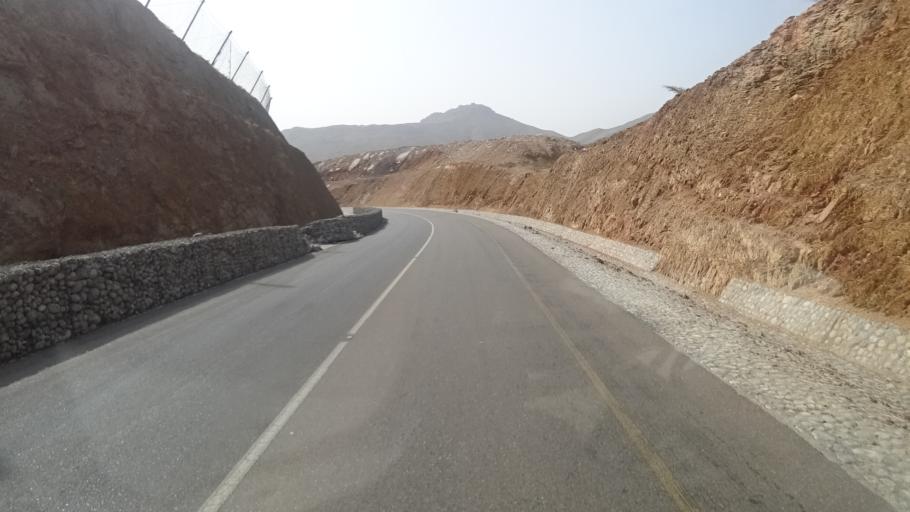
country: OM
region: Muhafazat ad Dakhiliyah
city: Nizwa
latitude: 23.0059
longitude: 57.5715
